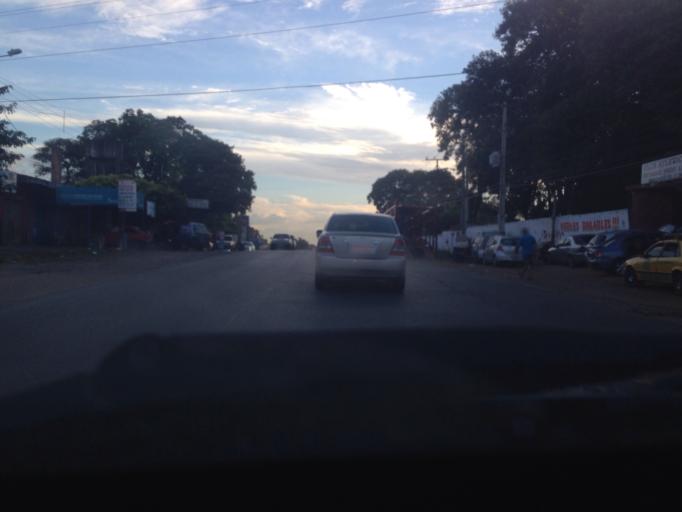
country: PY
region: Central
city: Lambare
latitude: -25.3489
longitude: -57.5905
